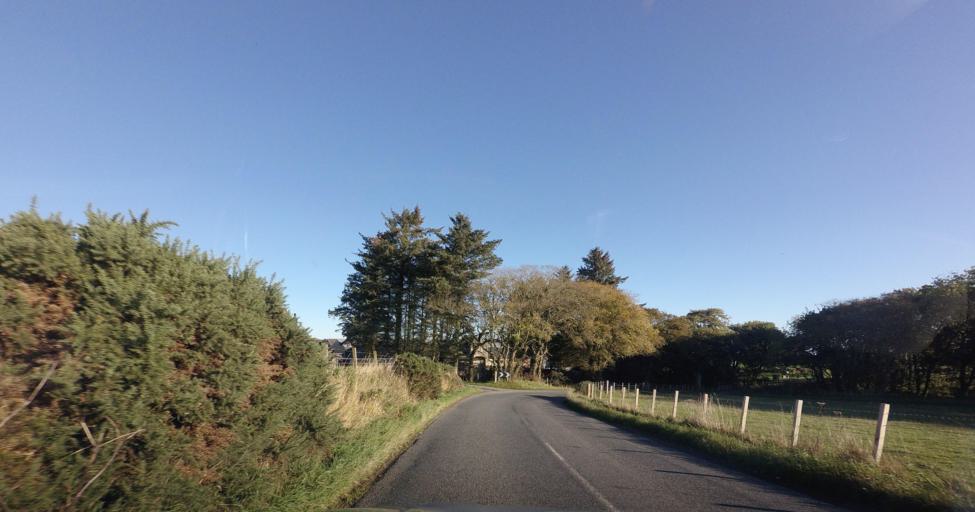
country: GB
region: Scotland
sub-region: Aberdeenshire
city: Rosehearty
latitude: 57.6763
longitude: -2.2917
